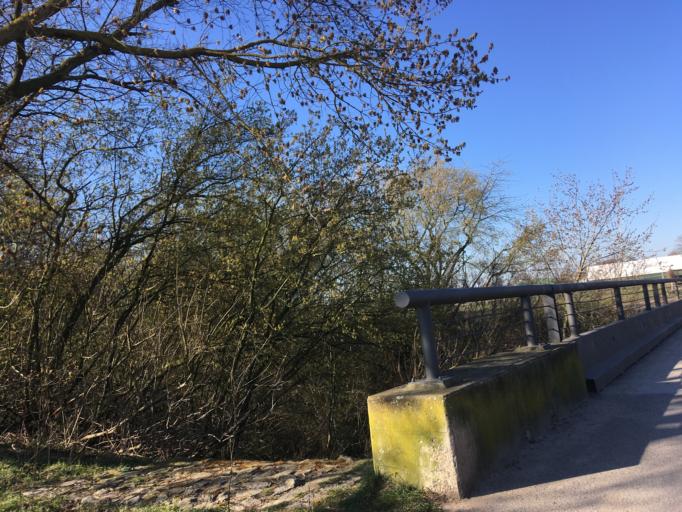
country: DE
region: Berlin
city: Blankenfelde
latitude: 52.6222
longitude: 13.4030
